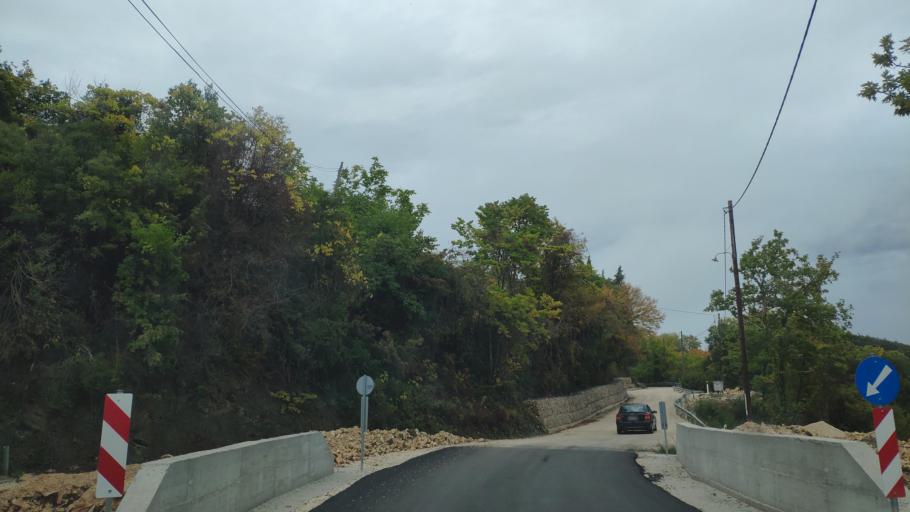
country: GR
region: Epirus
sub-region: Nomos Thesprotias
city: Paramythia
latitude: 39.4661
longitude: 20.6717
